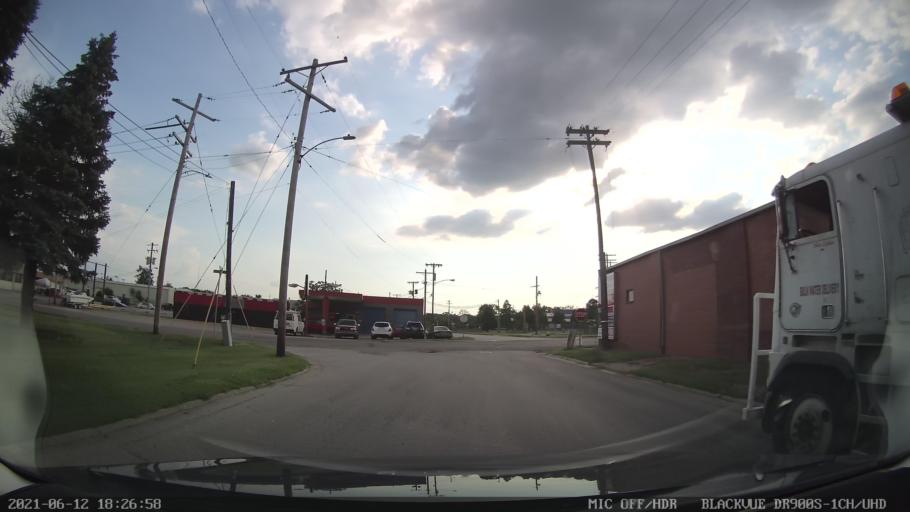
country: US
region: Illinois
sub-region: McLean County
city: Bloomington
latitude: 40.4704
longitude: -88.9771
